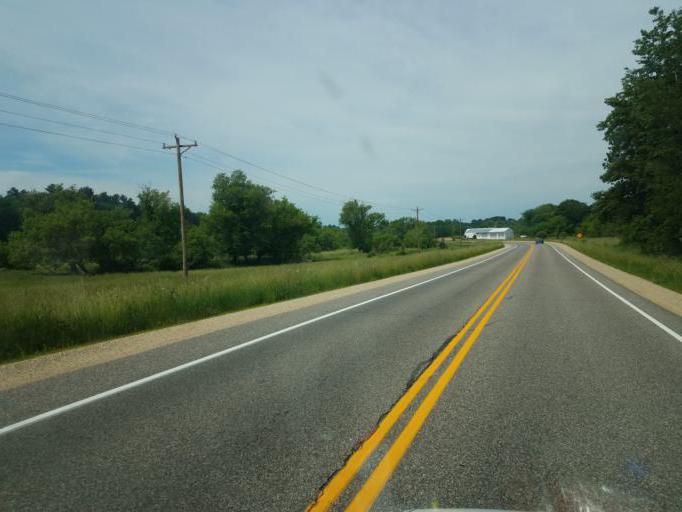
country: US
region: Wisconsin
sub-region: Juneau County
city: Elroy
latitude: 43.7643
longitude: -90.2575
